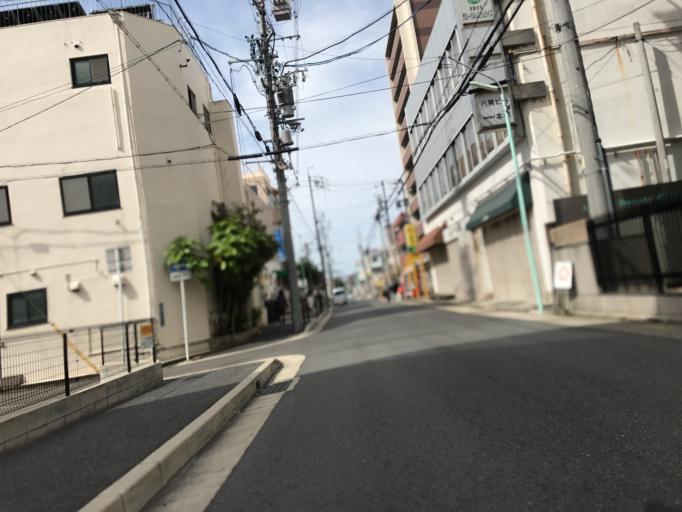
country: JP
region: Aichi
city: Nagoya-shi
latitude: 35.1684
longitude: 136.9297
